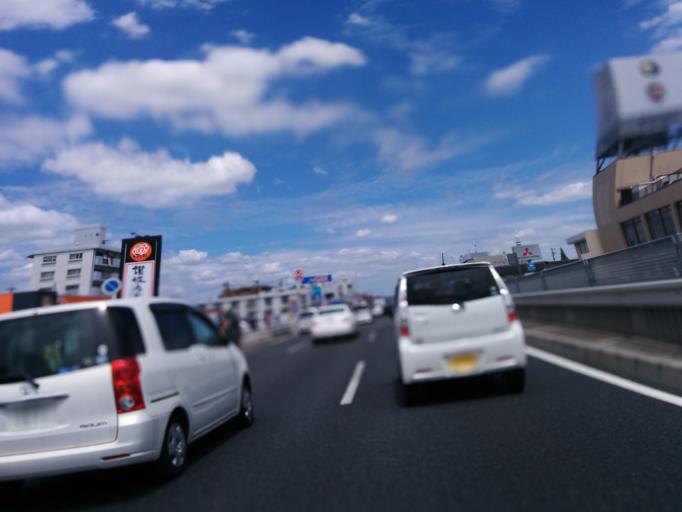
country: JP
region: Aichi
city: Kasugai
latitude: 35.2438
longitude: 136.9663
